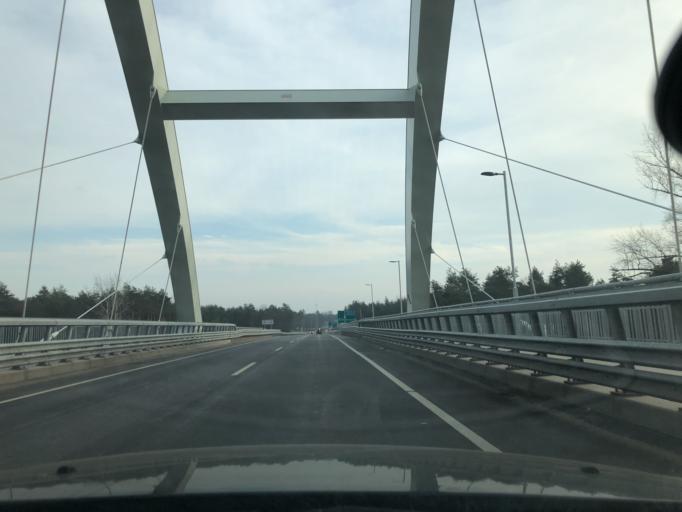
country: HU
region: Gyor-Moson-Sopron
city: Gyor
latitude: 47.7269
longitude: 17.7016
